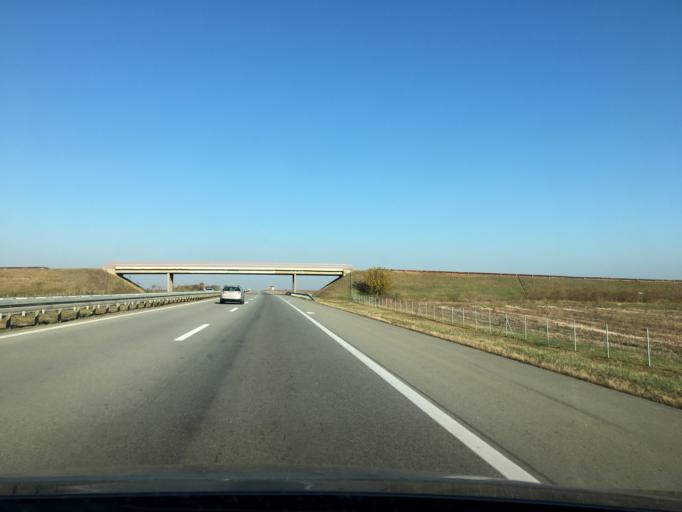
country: RS
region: Autonomna Pokrajina Vojvodina
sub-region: Juznobacki Okrug
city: Kovilj
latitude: 45.2072
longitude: 20.0697
